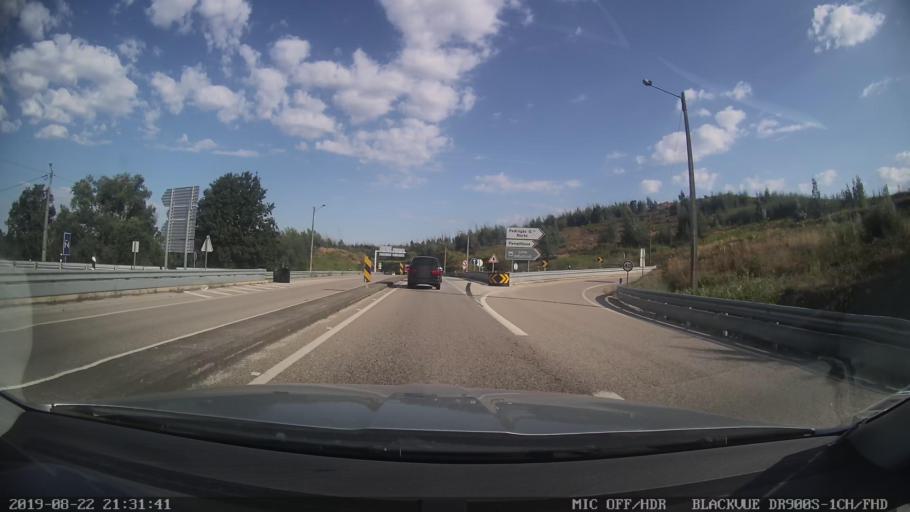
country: PT
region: Leiria
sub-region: Pedrogao Grande
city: Pedrogao Grande
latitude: 39.9227
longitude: -8.1560
